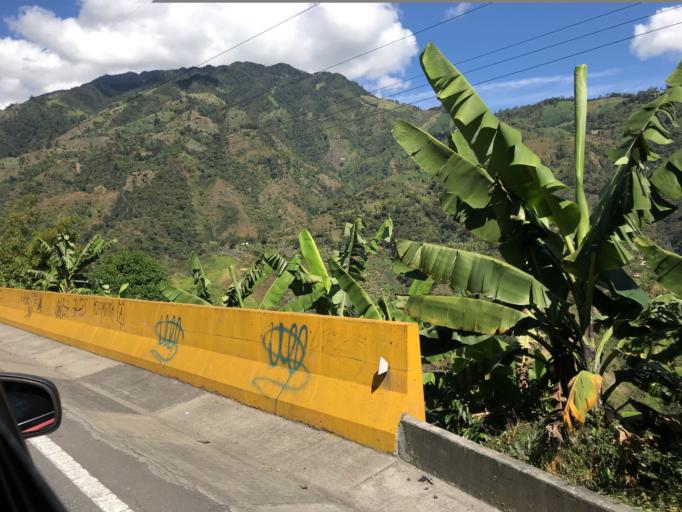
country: CO
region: Tolima
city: Cajamarca
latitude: 4.4422
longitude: -75.4066
